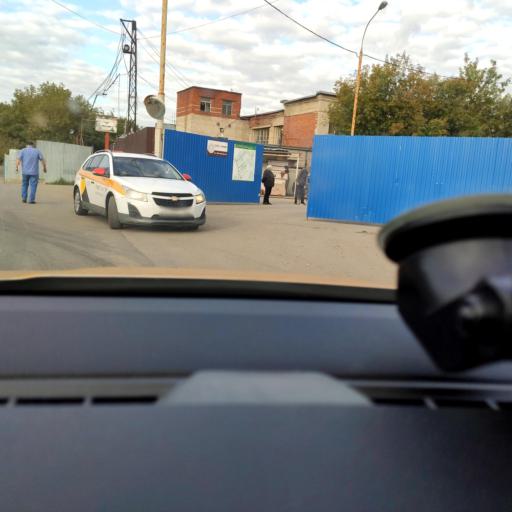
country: RU
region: Moscow
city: Metrogorodok
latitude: 55.8139
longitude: 37.7549
